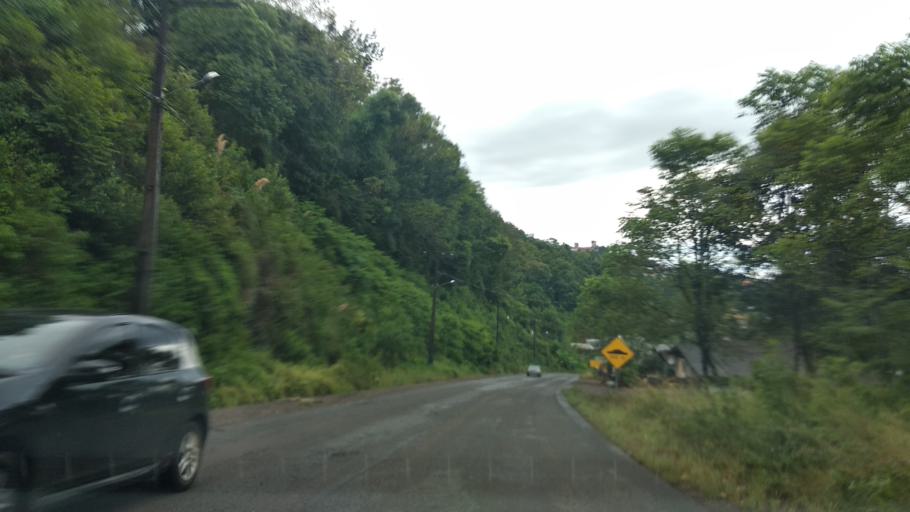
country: BR
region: Santa Catarina
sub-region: Videira
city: Videira
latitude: -27.0012
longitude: -51.1732
